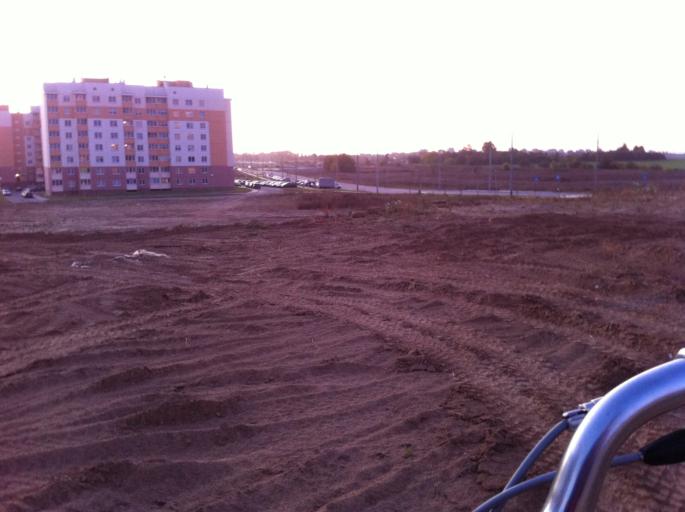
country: BY
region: Grodnenskaya
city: Hrodna
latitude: 53.7125
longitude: 23.8687
